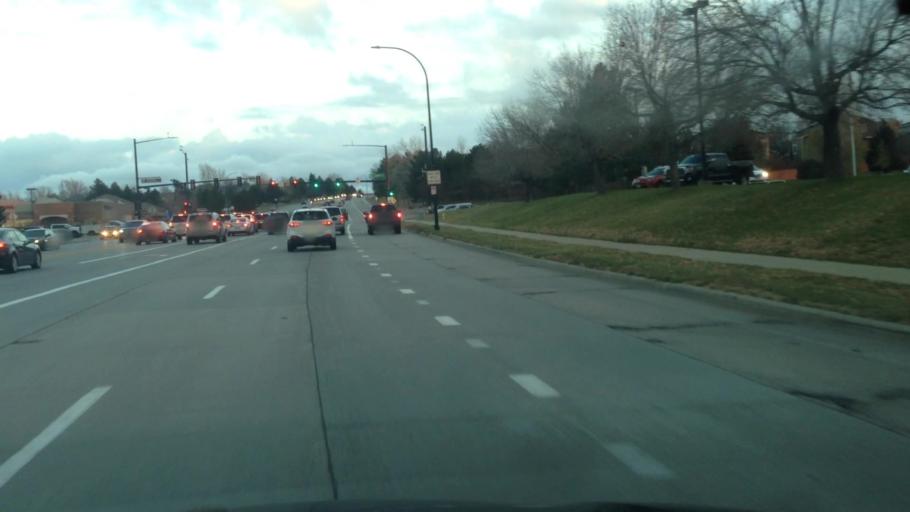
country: US
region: Colorado
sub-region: Douglas County
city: Carriage Club
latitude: 39.5427
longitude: -104.9148
